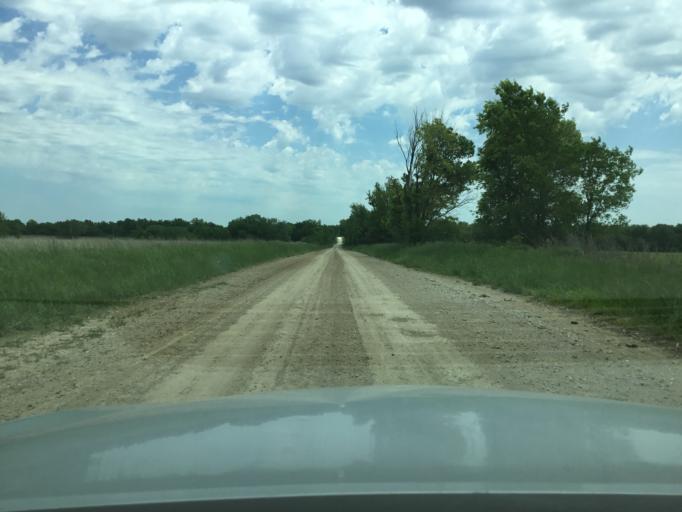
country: US
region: Kansas
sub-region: Montgomery County
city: Independence
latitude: 37.0951
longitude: -95.7972
